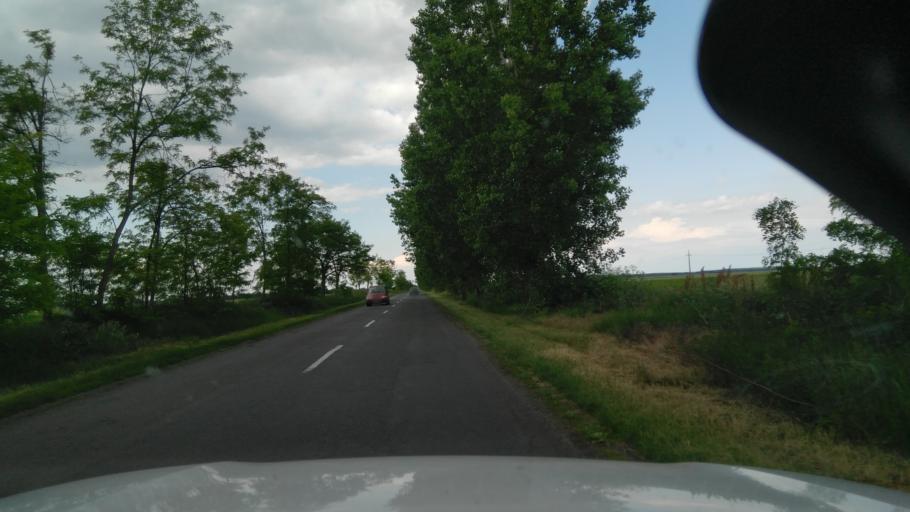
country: HU
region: Bekes
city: Magyarbanhegyes
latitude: 46.4564
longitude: 21.0010
